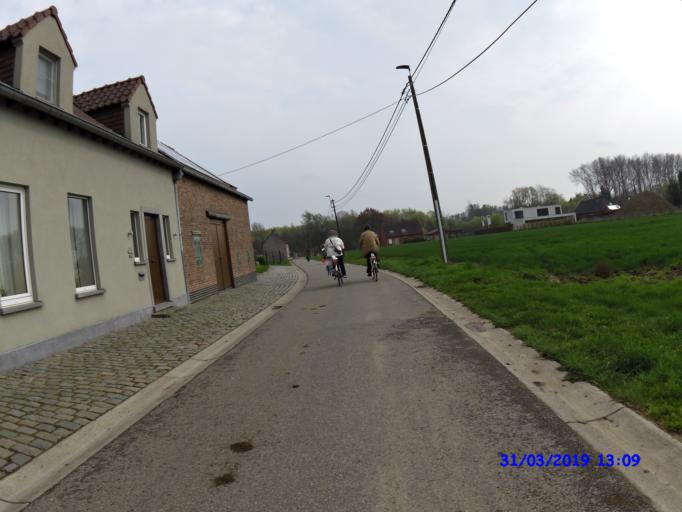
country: BE
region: Flanders
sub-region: Provincie Oost-Vlaanderen
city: Denderleeuw
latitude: 50.9266
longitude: 4.1233
